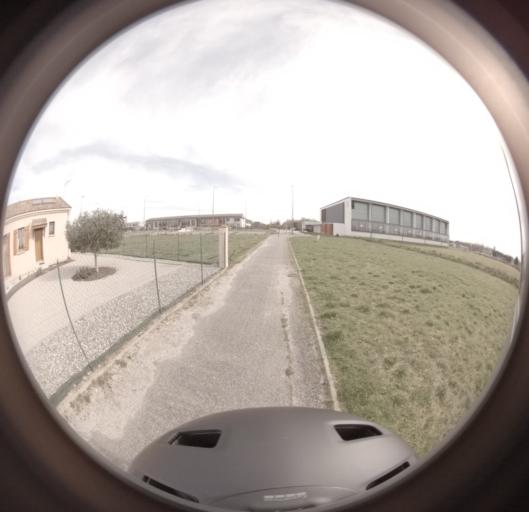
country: FR
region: Midi-Pyrenees
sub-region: Departement du Tarn-et-Garonne
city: Montech
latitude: 43.9595
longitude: 1.2494
